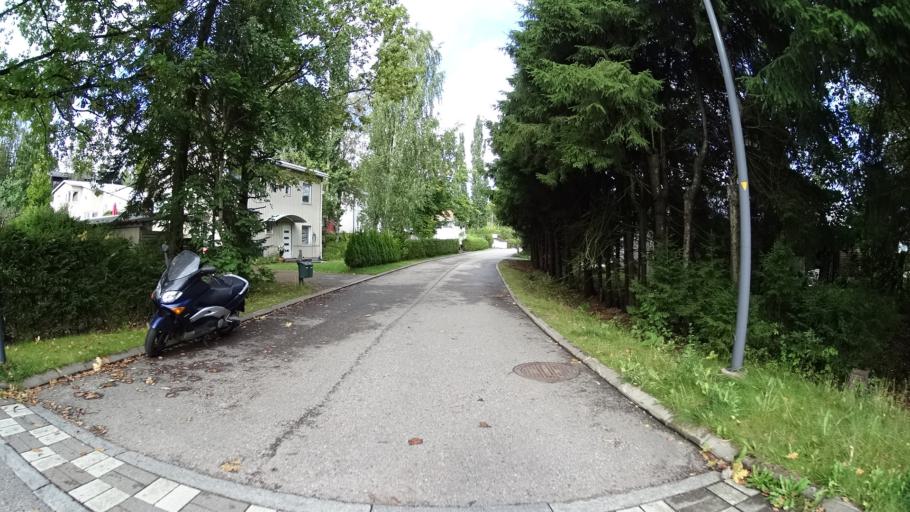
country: FI
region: Uusimaa
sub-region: Helsinki
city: Kilo
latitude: 60.1910
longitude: 24.7579
